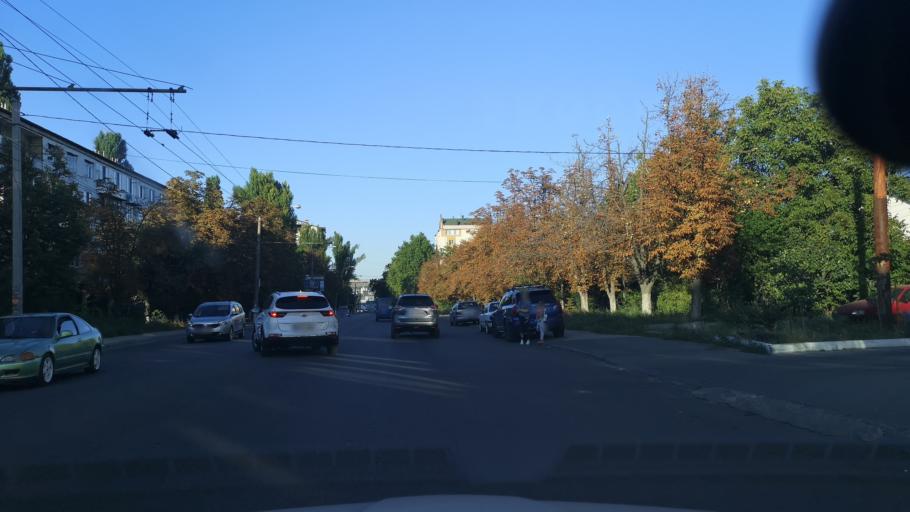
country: MD
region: Chisinau
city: Chisinau
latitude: 46.9837
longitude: 28.8792
